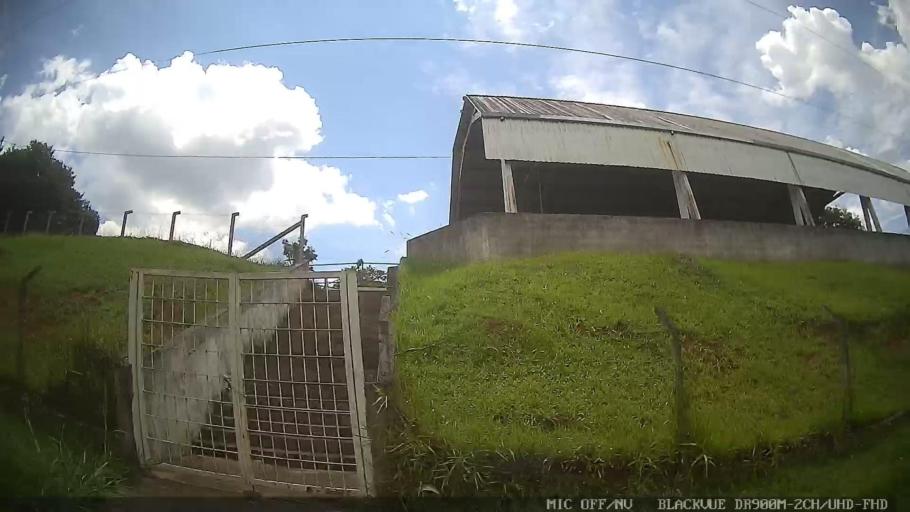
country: BR
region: Sao Paulo
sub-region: Jarinu
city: Jarinu
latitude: -23.0814
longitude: -46.6430
